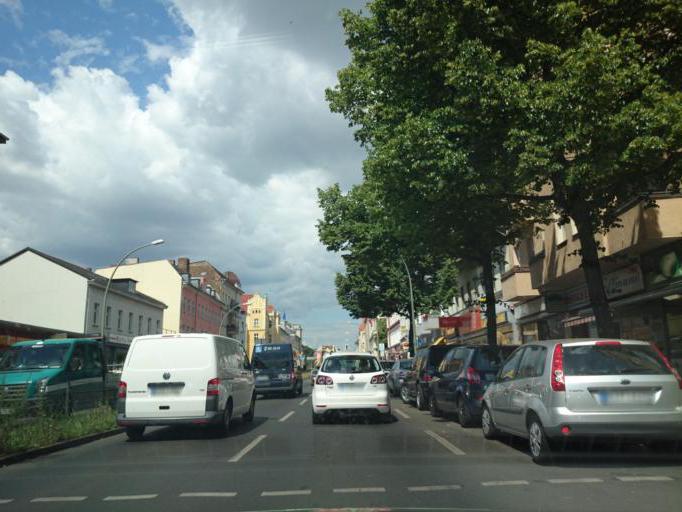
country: DE
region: Berlin
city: Tempelhof Bezirk
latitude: 52.4582
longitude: 13.3843
